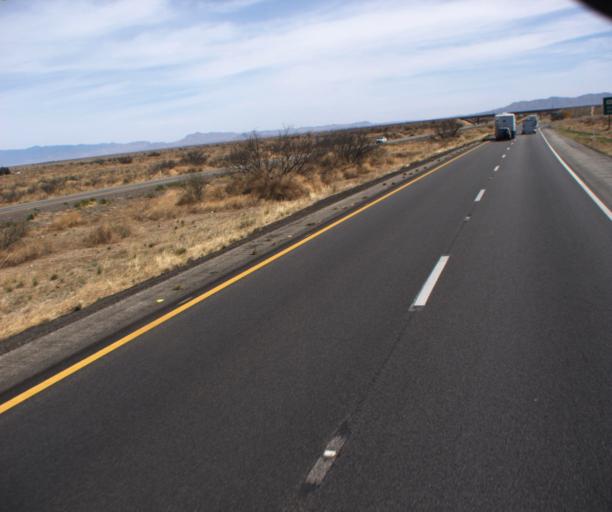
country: US
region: Arizona
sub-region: Cochise County
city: Willcox
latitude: 32.1737
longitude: -109.9538
